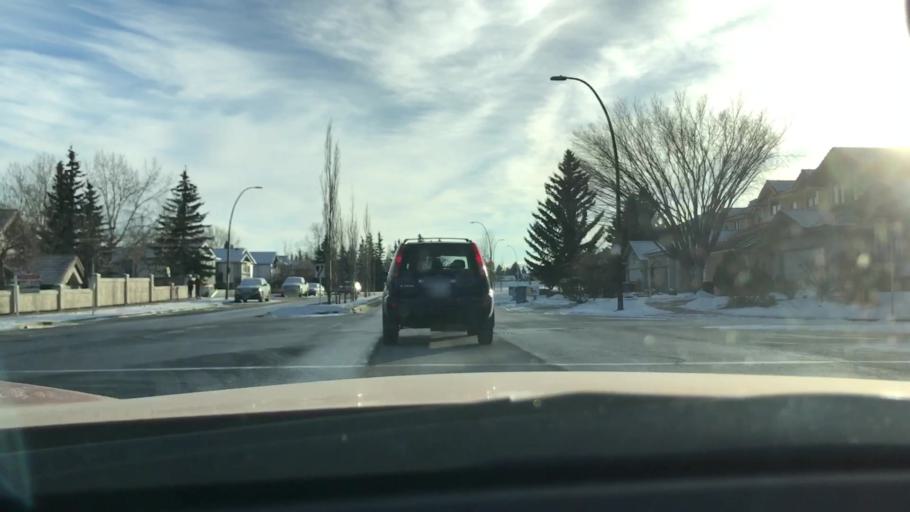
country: CA
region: Alberta
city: Calgary
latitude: 51.0341
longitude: -114.1668
